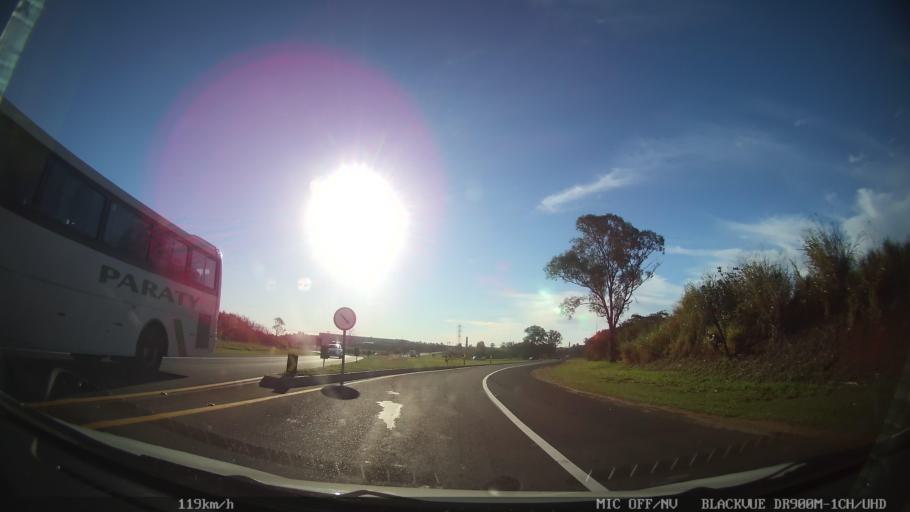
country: BR
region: Sao Paulo
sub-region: Americo Brasiliense
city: Americo Brasiliense
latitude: -21.7585
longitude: -48.1186
